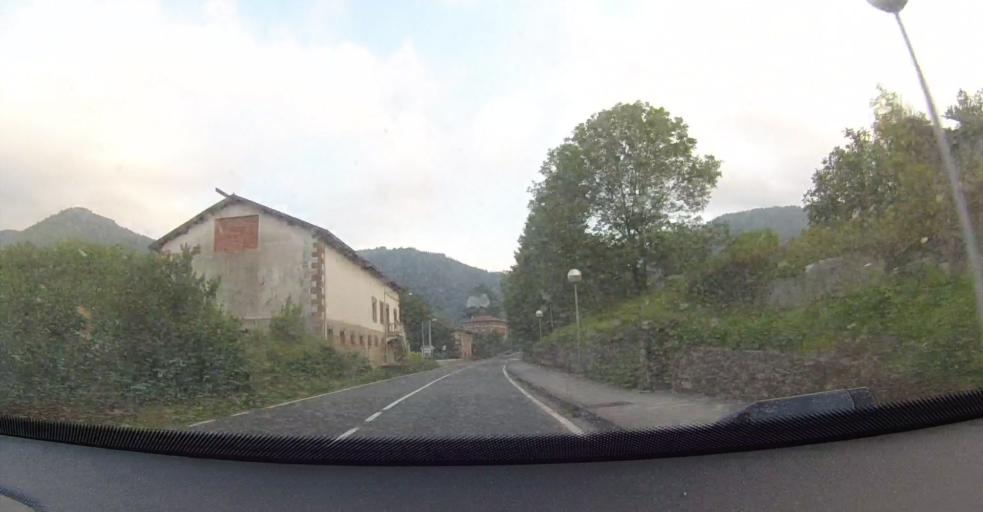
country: ES
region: Basque Country
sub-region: Bizkaia
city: Sopuerta
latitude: 43.2560
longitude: -3.1536
